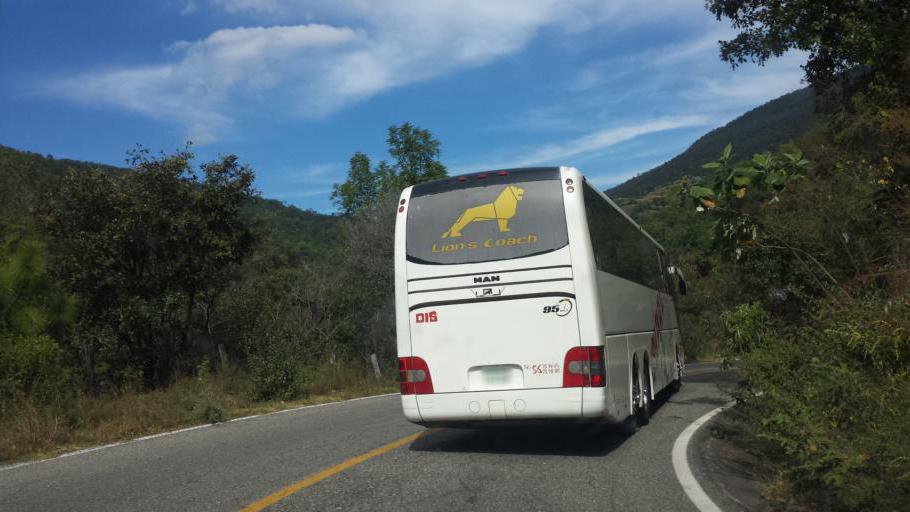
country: MX
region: Oaxaca
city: San Francisco Sola
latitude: 16.4536
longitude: -97.0305
